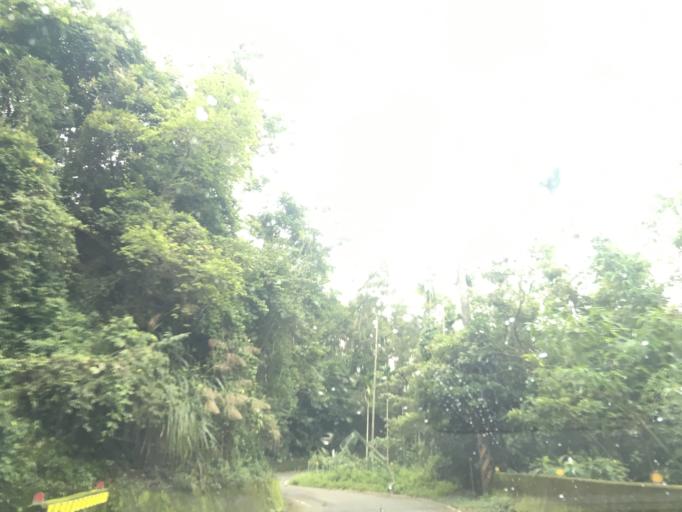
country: TW
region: Taiwan
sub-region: Yunlin
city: Douliu
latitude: 23.5691
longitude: 120.6321
